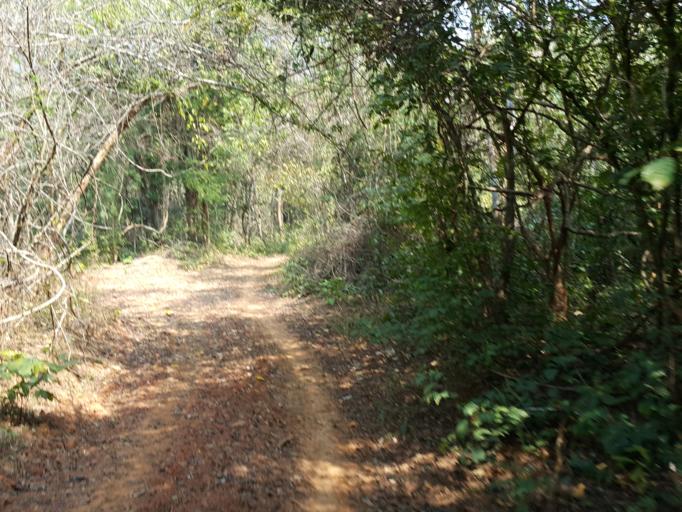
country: TH
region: Sukhothai
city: Thung Saliam
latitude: 17.3246
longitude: 99.5003
